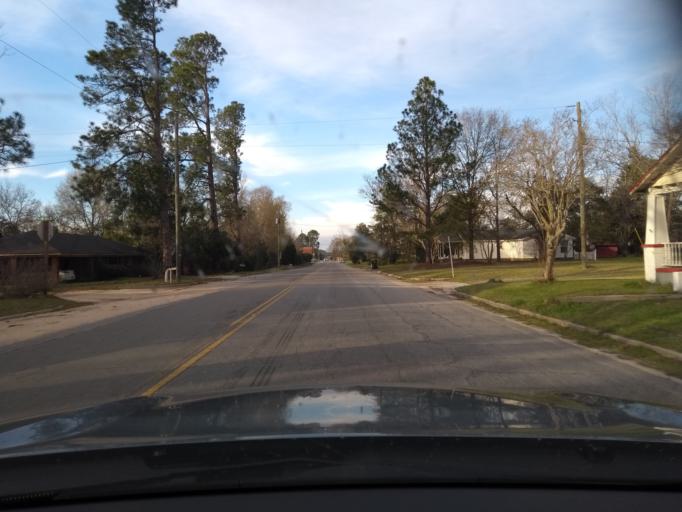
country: US
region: Georgia
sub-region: Bulloch County
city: Brooklet
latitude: 32.2615
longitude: -81.7617
